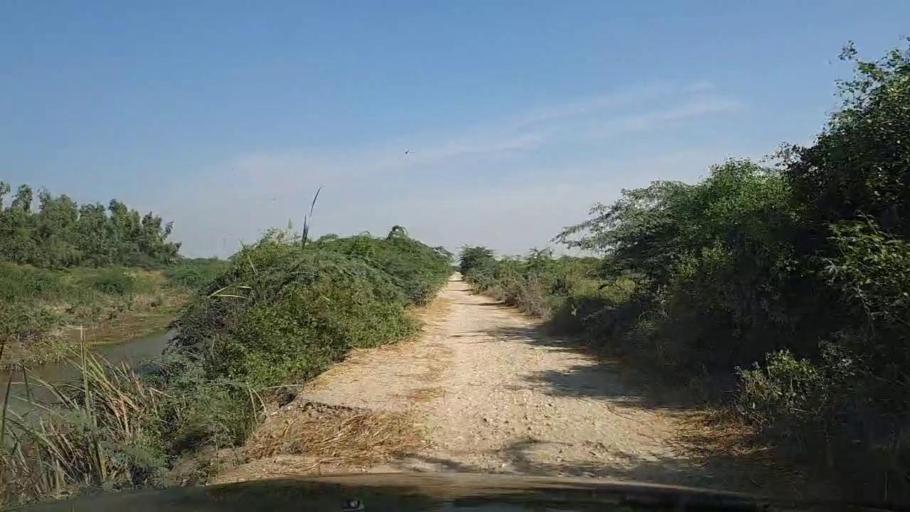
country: PK
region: Sindh
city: Thatta
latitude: 24.7112
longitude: 67.7814
